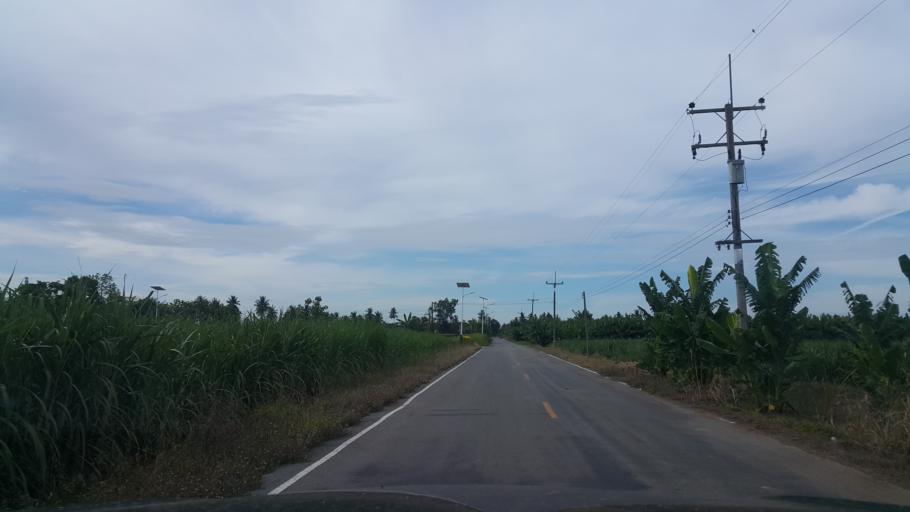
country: TH
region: Sukhothai
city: Sawankhalok
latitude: 17.2659
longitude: 99.9089
